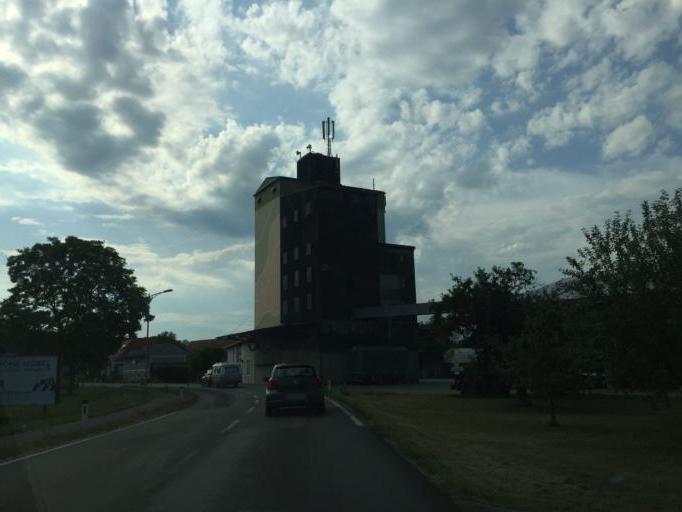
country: AT
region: Styria
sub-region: Politischer Bezirk Suedoststeiermark
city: Deutsch Goritz
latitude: 46.7295
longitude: 15.8535
